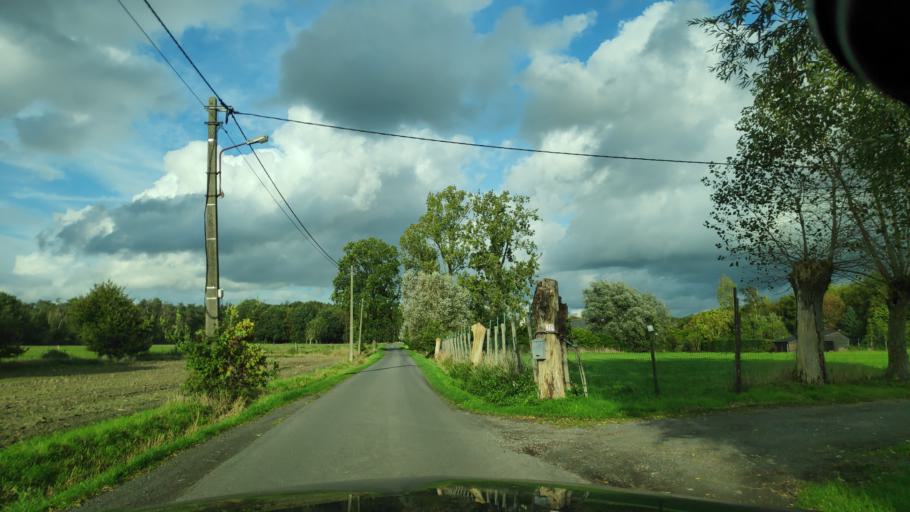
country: BE
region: Flanders
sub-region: Provincie Oost-Vlaanderen
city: Knesselare
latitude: 51.1456
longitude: 3.4440
